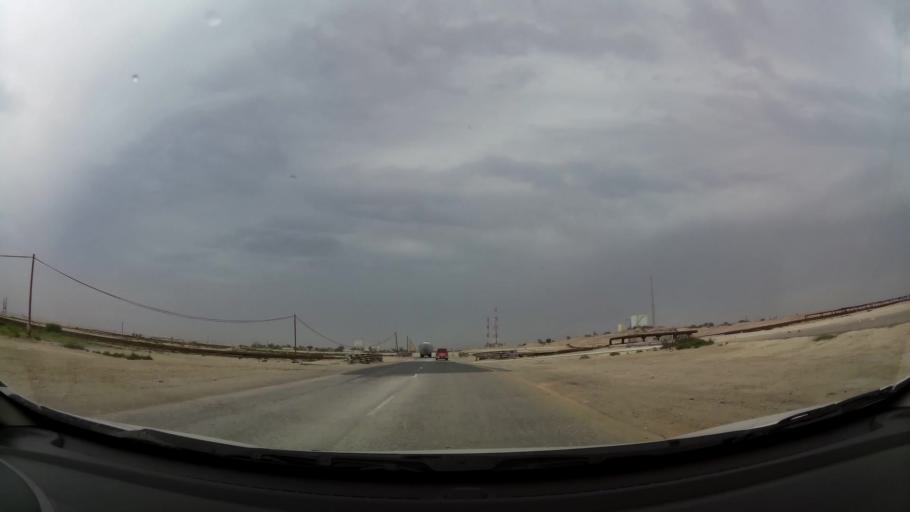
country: BH
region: Central Governorate
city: Dar Kulayb
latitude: 26.0761
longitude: 50.5510
